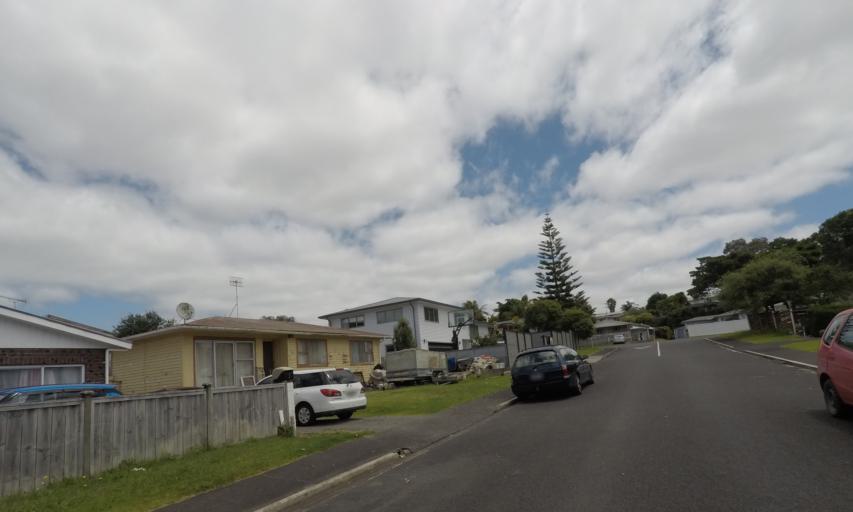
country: NZ
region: Auckland
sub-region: Auckland
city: North Shore
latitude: -36.7902
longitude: 174.7046
